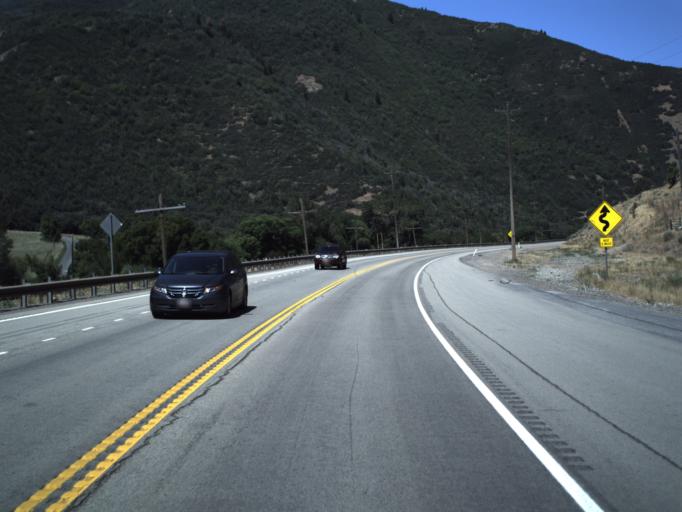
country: US
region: Utah
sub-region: Utah County
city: Mapleton
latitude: 40.0421
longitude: -111.5443
